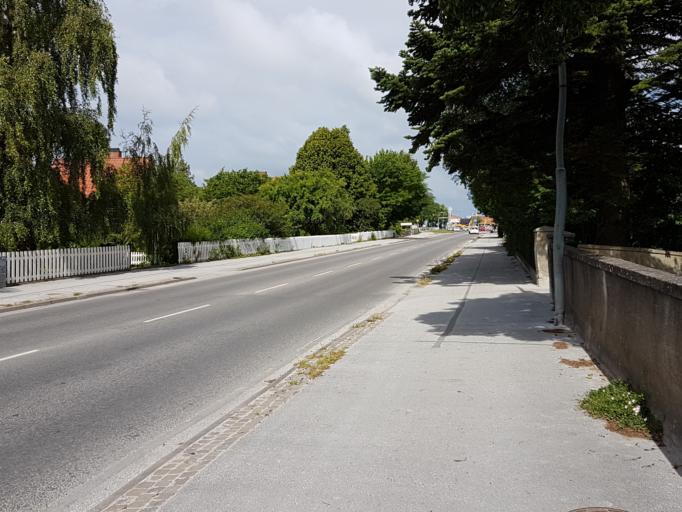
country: SE
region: Gotland
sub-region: Gotland
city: Visby
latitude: 57.6334
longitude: 18.3101
